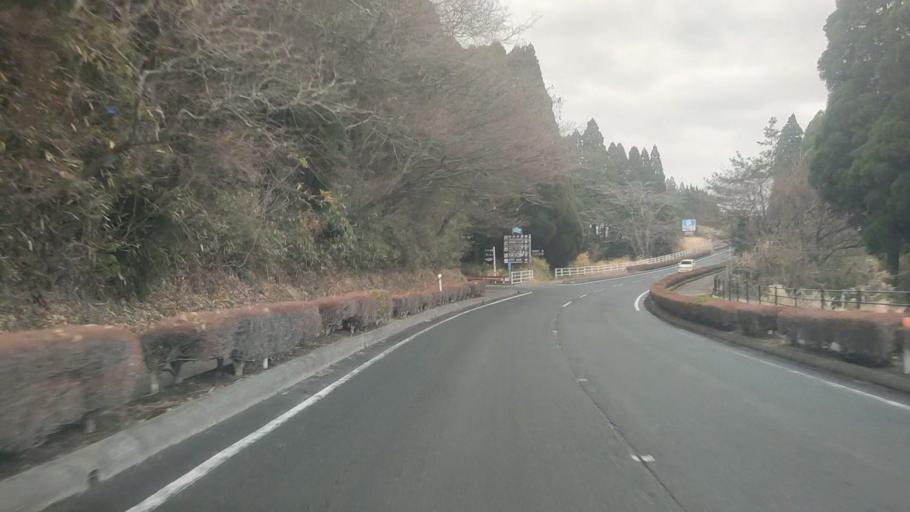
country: JP
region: Kumamoto
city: Aso
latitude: 32.8335
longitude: 131.0723
